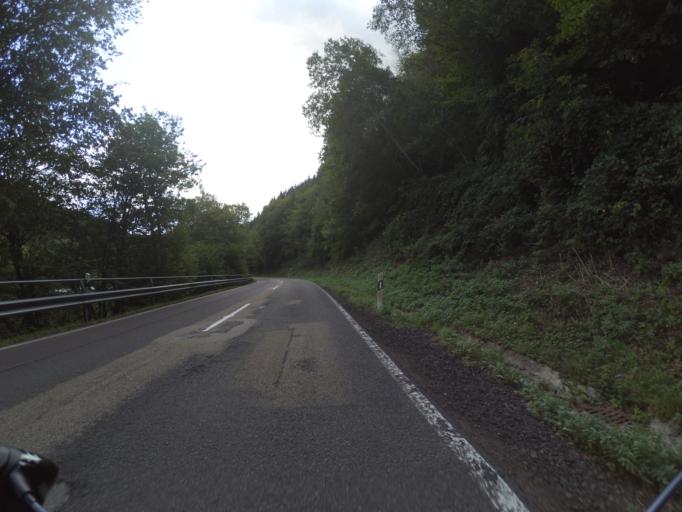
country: DE
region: Rheinland-Pfalz
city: Budlich
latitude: 49.7958
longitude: 6.8981
